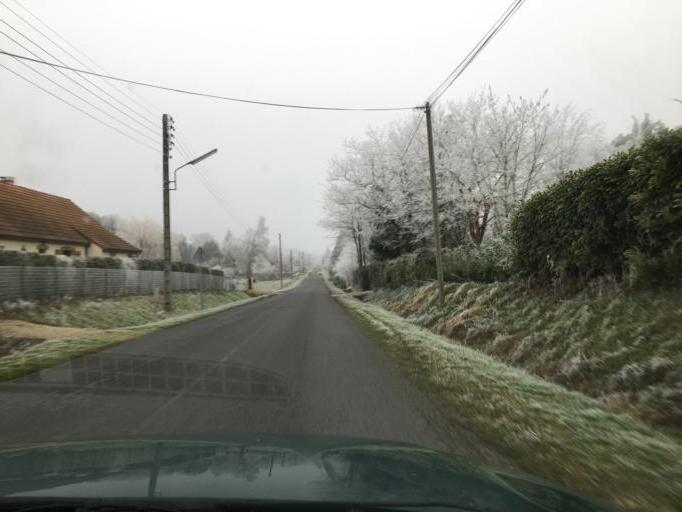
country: FR
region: Centre
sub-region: Departement du Loir-et-Cher
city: Chaumont-sur-Tharonne
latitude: 47.6317
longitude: 1.8504
